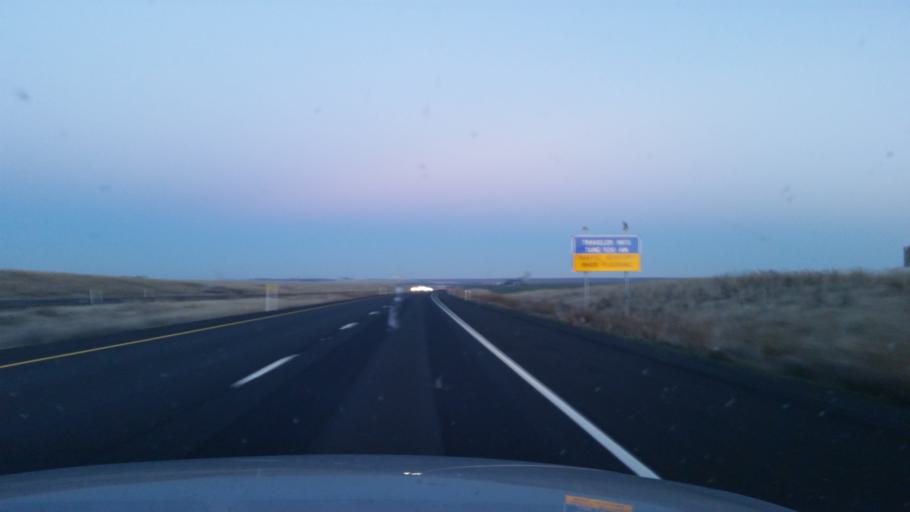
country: US
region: Washington
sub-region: Adams County
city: Ritzville
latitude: 47.1111
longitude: -118.4524
